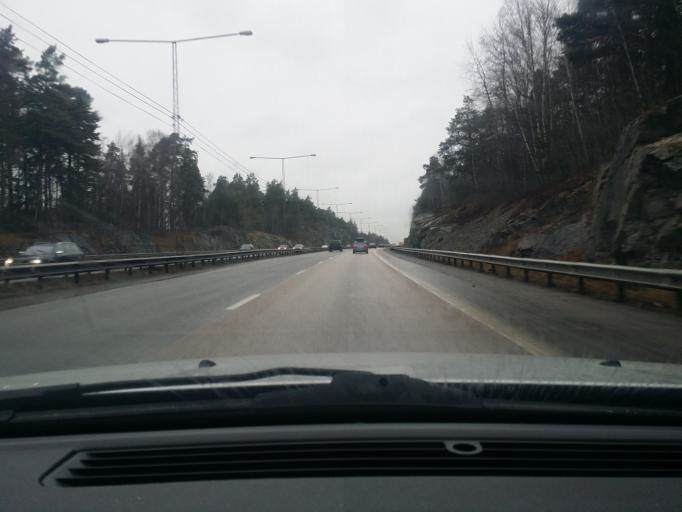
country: SE
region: Stockholm
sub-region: Jarfalla Kommun
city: Jakobsberg
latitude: 59.4353
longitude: 17.8453
